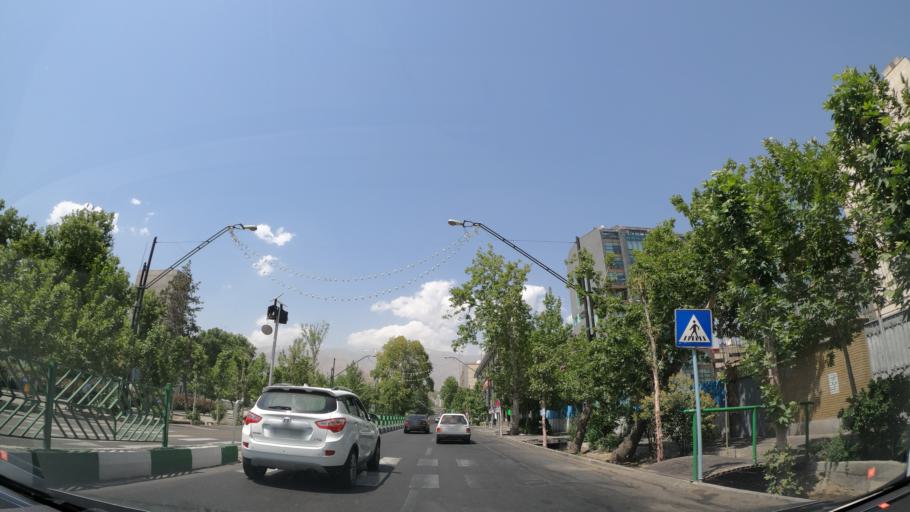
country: IR
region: Tehran
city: Tajrish
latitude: 35.7786
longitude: 51.4136
